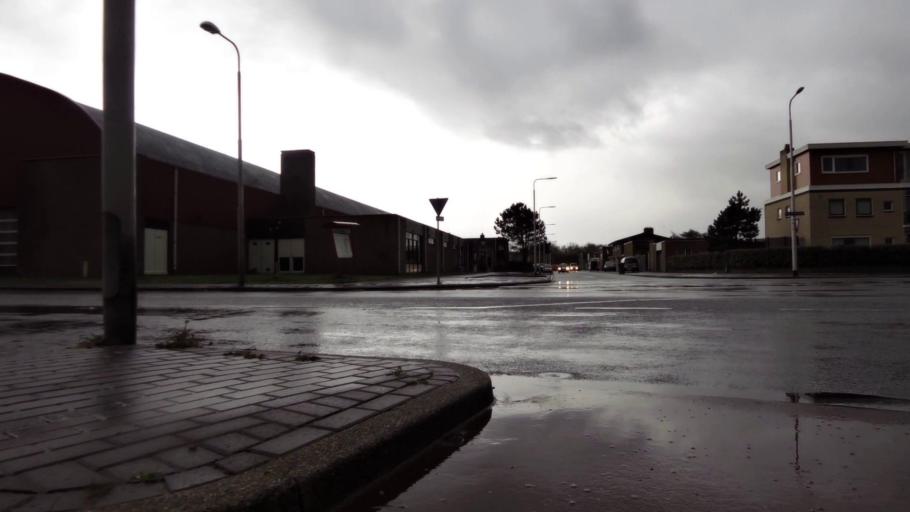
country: NL
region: North Holland
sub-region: Gemeente Velsen
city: Velsen-Zuid
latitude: 52.4547
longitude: 4.5920
